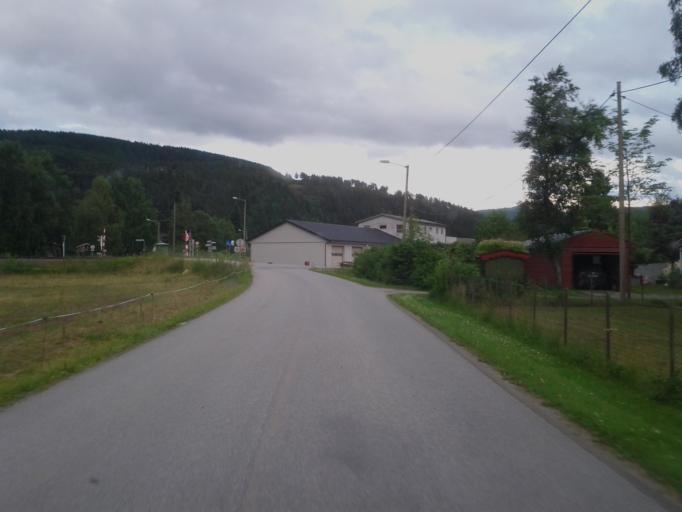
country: NO
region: Sor-Trondelag
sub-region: Midtre Gauldal
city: Storen
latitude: 63.0456
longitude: 10.2868
